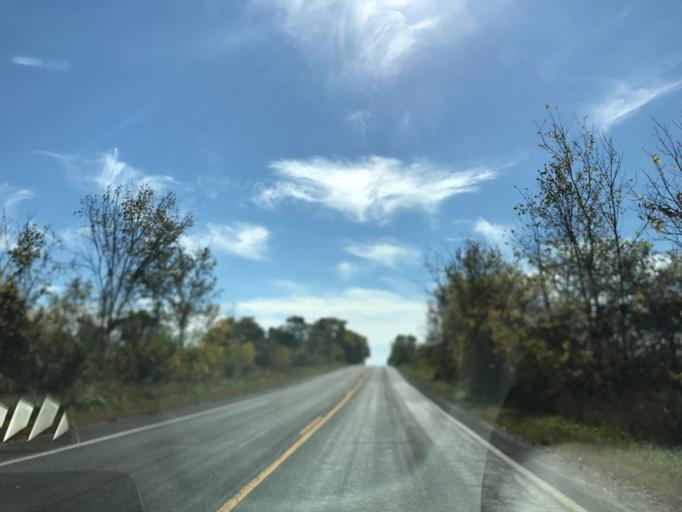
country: US
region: Michigan
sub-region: Oakland County
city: South Lyon
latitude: 42.3607
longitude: -83.6626
